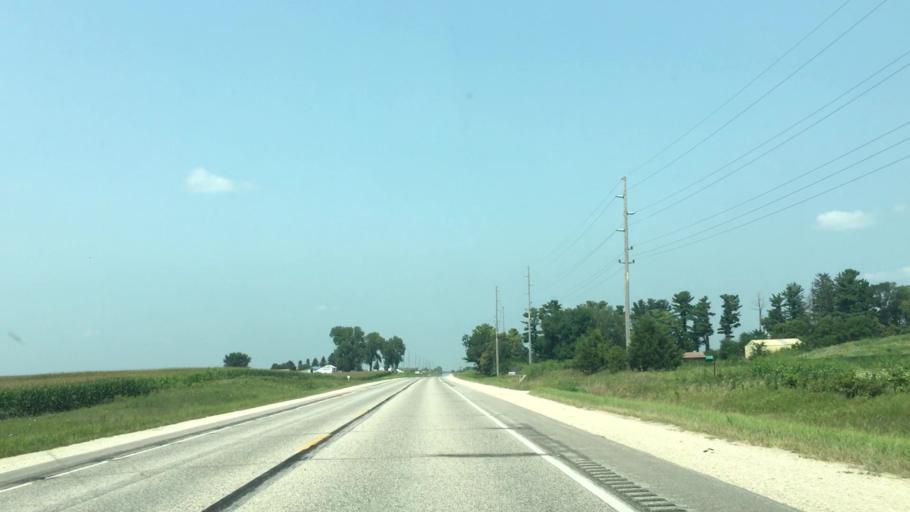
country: US
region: Iowa
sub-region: Fayette County
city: Fayette
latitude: 42.8783
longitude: -91.8105
